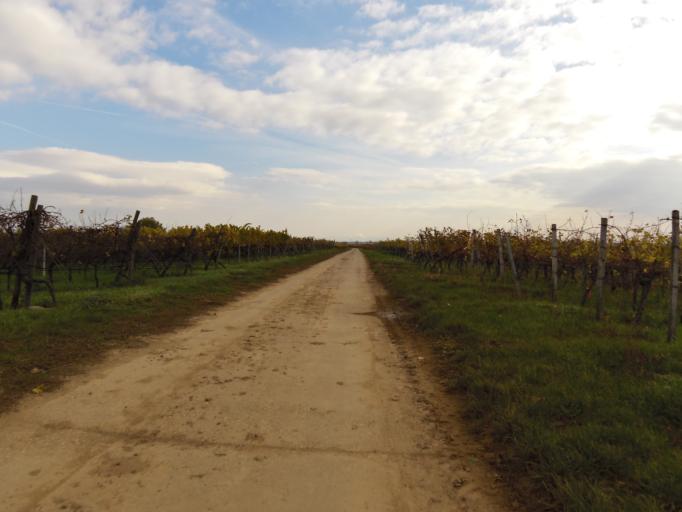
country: DE
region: Rheinland-Pfalz
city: Gonnheim
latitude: 49.4415
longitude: 8.2413
